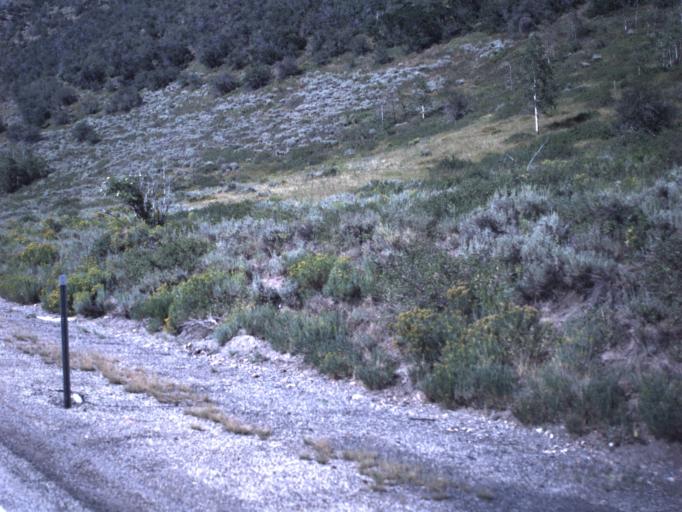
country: US
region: Utah
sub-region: Wasatch County
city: Heber
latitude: 40.3411
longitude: -111.2642
